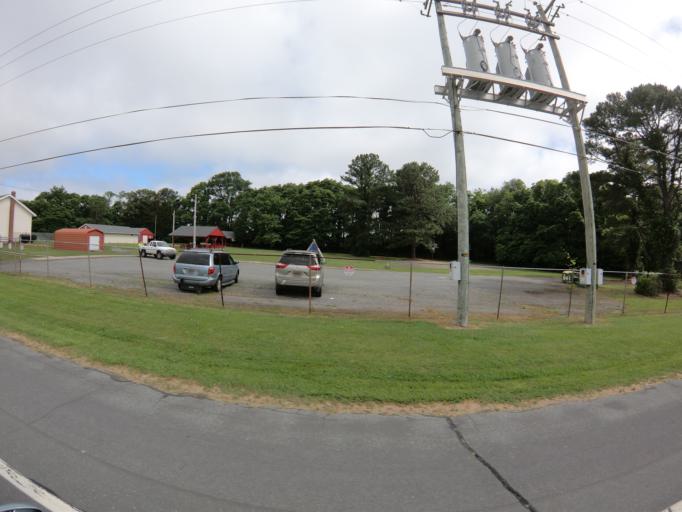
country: US
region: Delaware
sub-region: Kent County
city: Riverview
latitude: 39.0116
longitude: -75.5099
